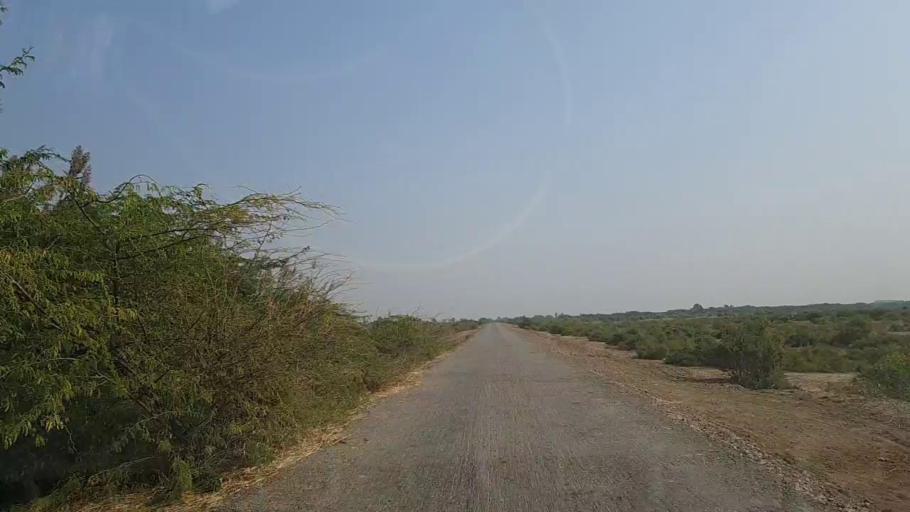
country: PK
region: Sindh
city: Keti Bandar
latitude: 24.2310
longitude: 67.6527
